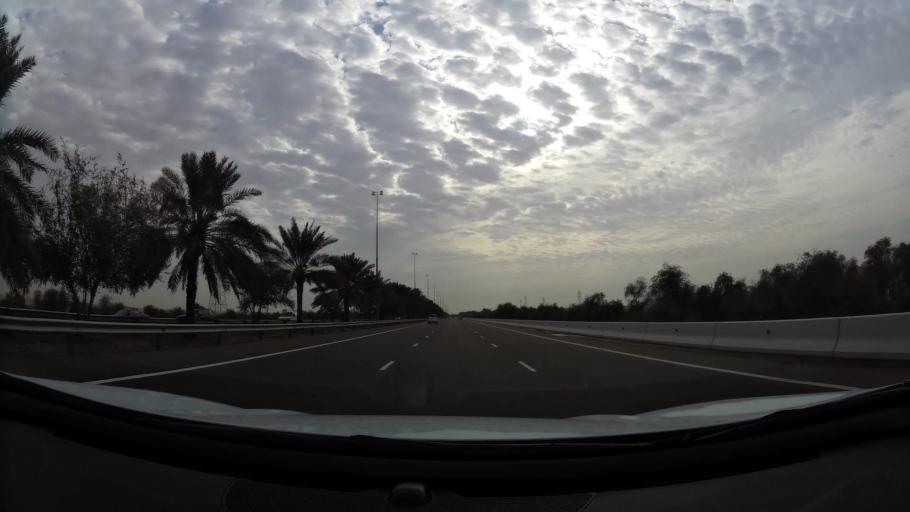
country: AE
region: Abu Dhabi
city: Al Ain
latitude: 24.1732
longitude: 55.2103
